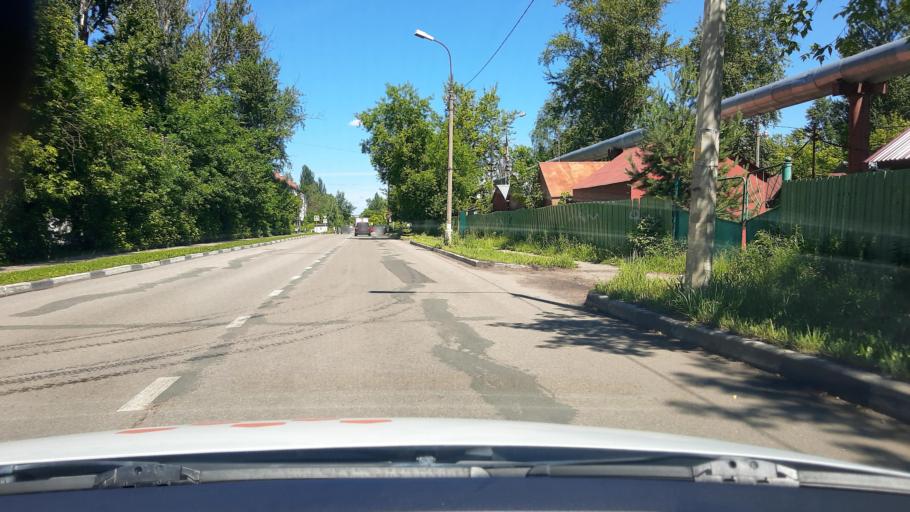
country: RU
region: Moskovskaya
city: Elektrostal'
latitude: 55.7973
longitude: 38.4439
